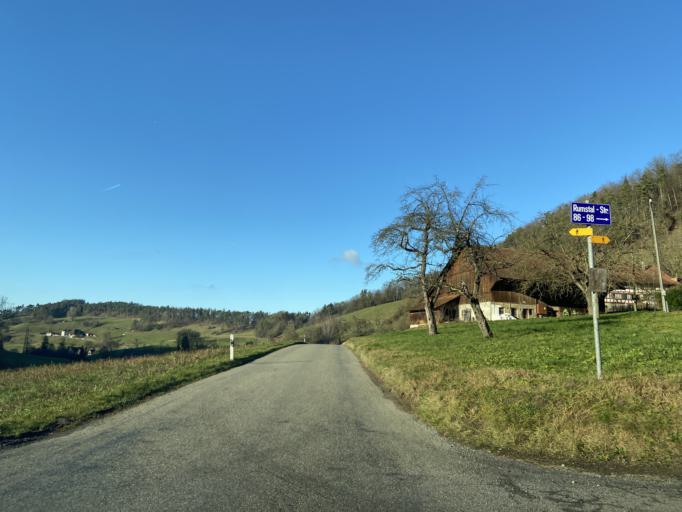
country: CH
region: Zurich
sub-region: Bezirk Winterthur
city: Wuelflingen (Kreis 6) / Niederfeld
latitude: 47.5035
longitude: 8.6610
